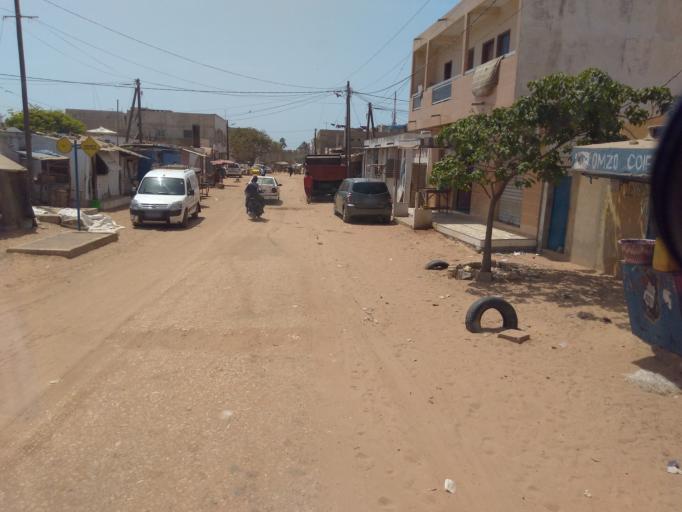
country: SN
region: Dakar
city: Pikine
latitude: 14.7889
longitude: -17.3396
